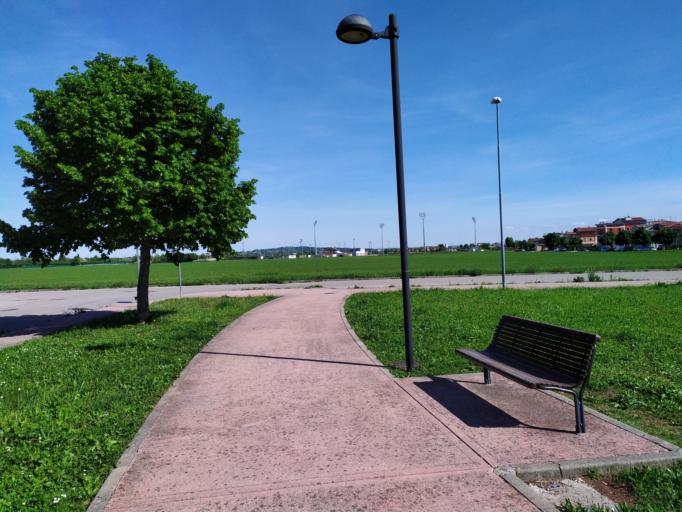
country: IT
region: Veneto
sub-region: Provincia di Vicenza
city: Thiene
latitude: 45.7004
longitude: 11.4923
